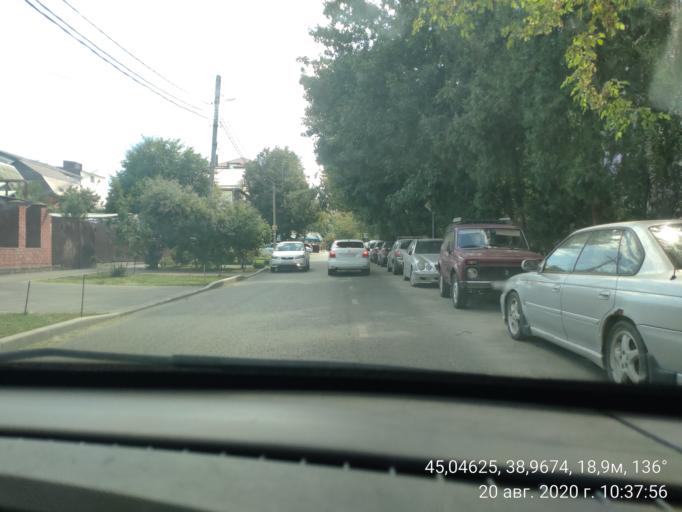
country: RU
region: Krasnodarskiy
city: Krasnodar
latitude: 45.0463
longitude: 38.9672
